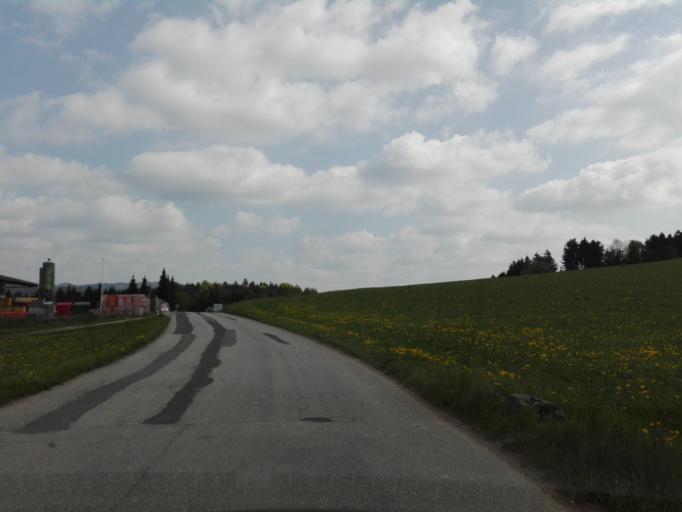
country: AT
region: Upper Austria
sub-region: Politischer Bezirk Perg
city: Bad Kreuzen
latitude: 48.2681
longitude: 14.7201
